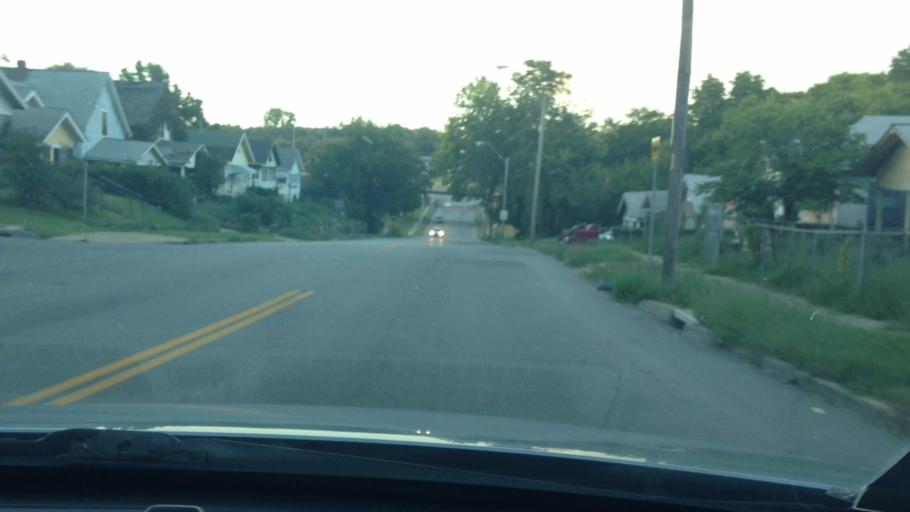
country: US
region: Missouri
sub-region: Jackson County
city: Kansas City
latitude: 39.0709
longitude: -94.5344
